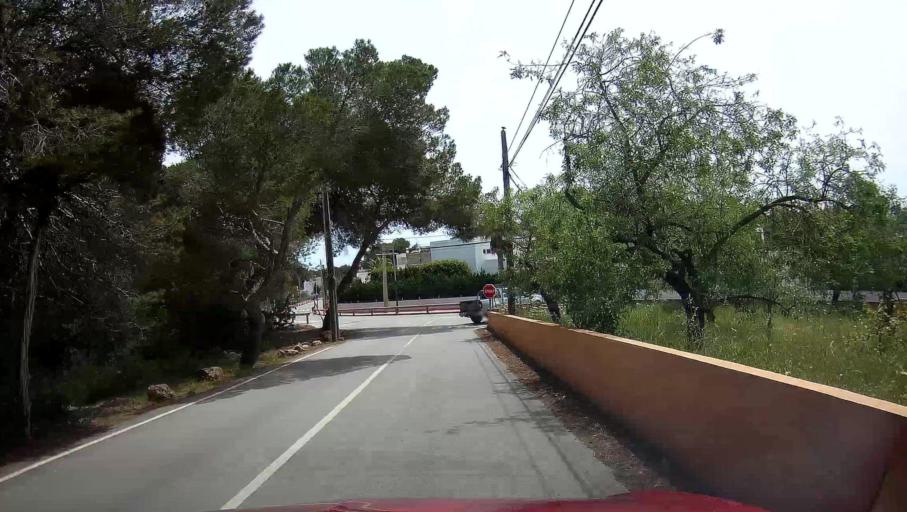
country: ES
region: Balearic Islands
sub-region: Illes Balears
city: Santa Eularia des Riu
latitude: 39.0051
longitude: 1.5713
